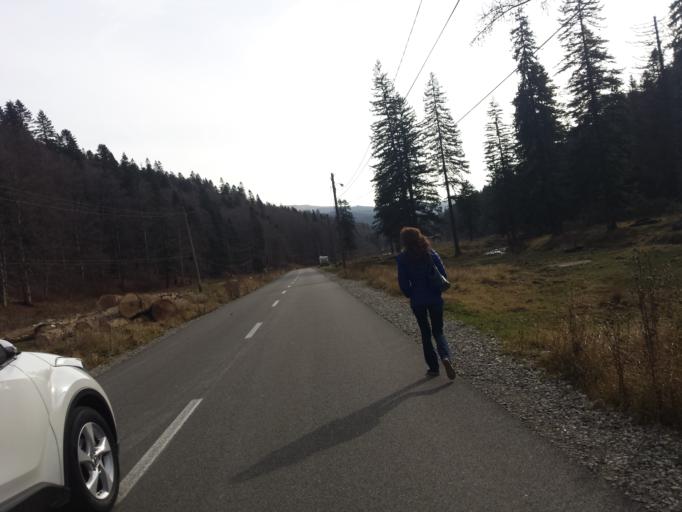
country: RO
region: Prahova
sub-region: Oras Azuga
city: Azuga
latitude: 45.4463
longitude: 25.5228
